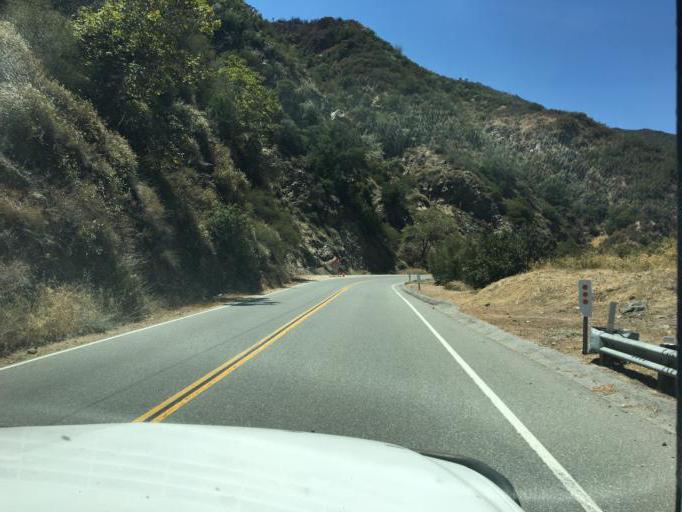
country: US
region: California
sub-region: Los Angeles County
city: Glendora
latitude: 34.2036
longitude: -117.8648
